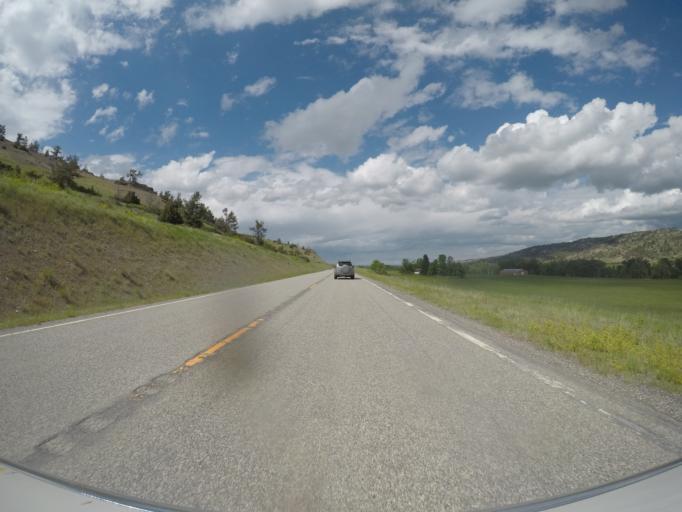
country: US
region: Montana
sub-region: Sweet Grass County
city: Big Timber
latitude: 45.7350
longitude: -109.9989
